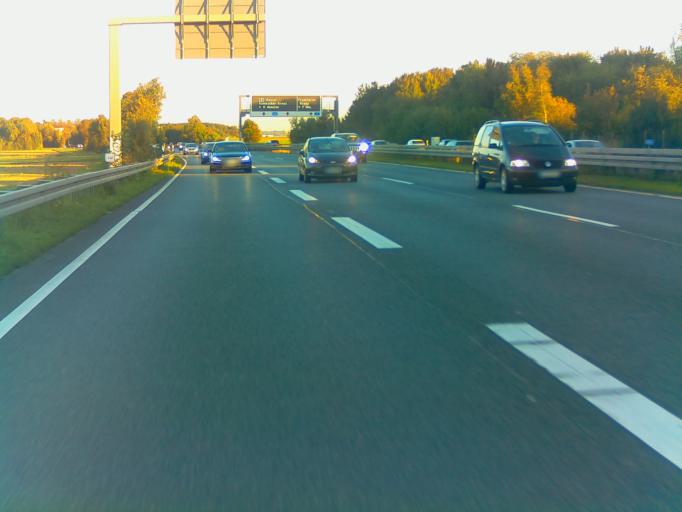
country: DE
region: Hesse
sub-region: Regierungsbezirk Darmstadt
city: Bad Homburg vor der Hoehe
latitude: 50.2046
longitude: 8.6293
